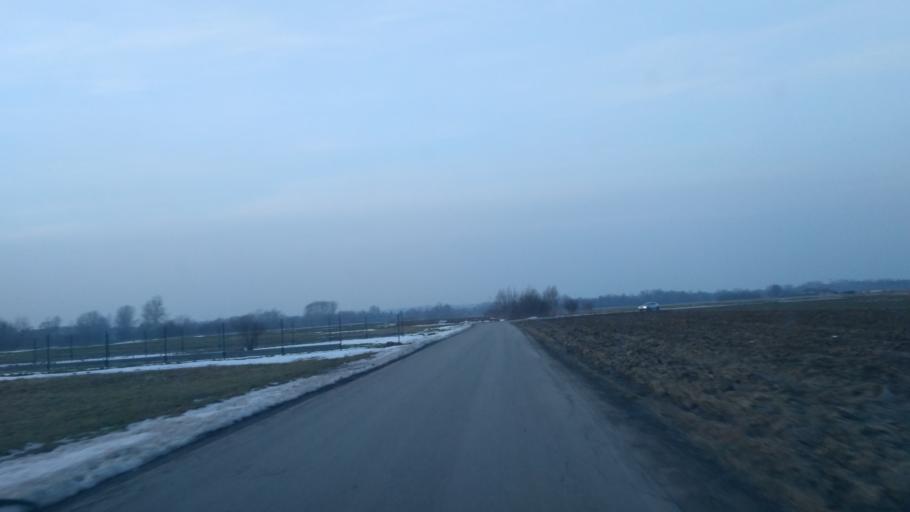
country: PL
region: Subcarpathian Voivodeship
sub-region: Powiat rzeszowski
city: Boguchwala
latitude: 49.9751
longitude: 21.9628
